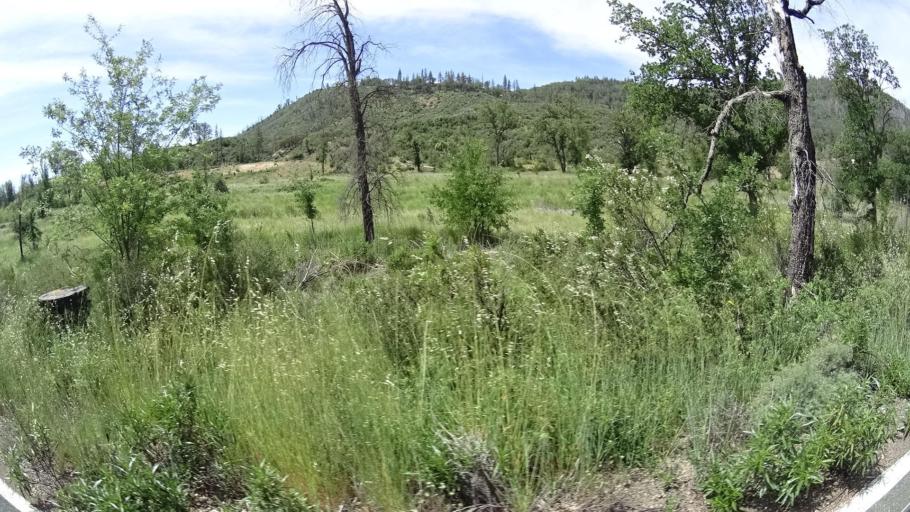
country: US
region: California
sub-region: Lake County
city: Cobb
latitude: 38.8763
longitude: -122.6823
